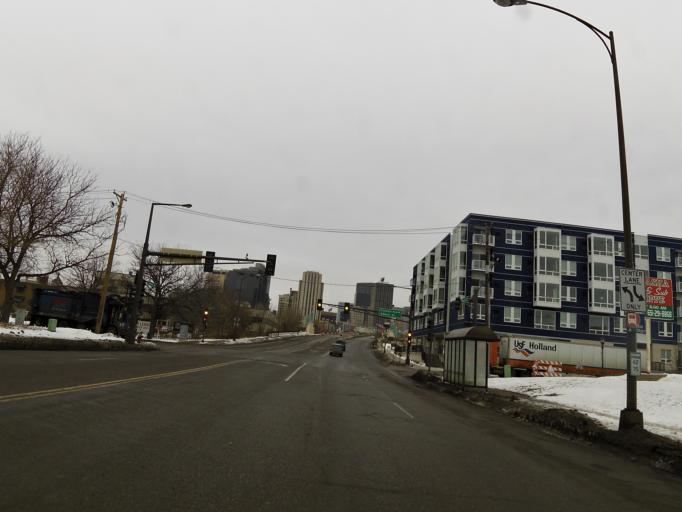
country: US
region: Minnesota
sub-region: Ramsey County
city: Saint Paul
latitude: 44.9390
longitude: -93.0891
